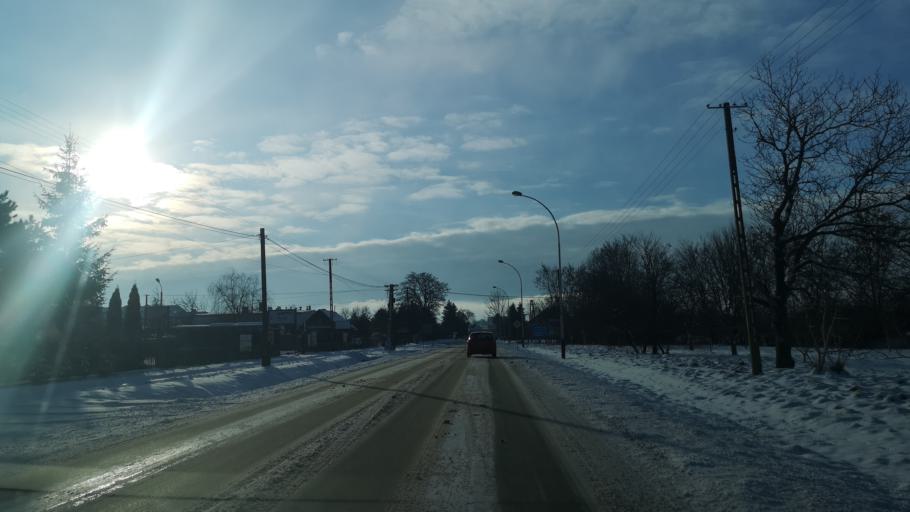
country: PL
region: Subcarpathian Voivodeship
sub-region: Powiat przeworski
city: Gorliczyna
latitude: 50.0792
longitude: 22.4933
